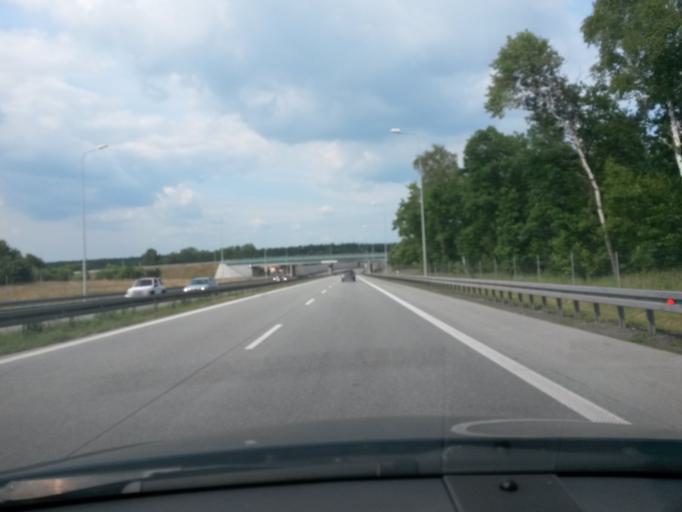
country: PL
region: Lodz Voivodeship
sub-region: Powiat rawski
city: Rawa Mazowiecka
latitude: 51.8240
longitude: 20.3223
